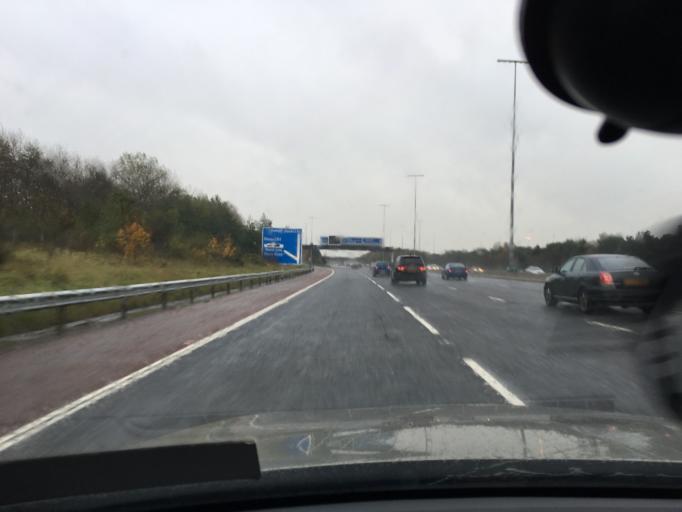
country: GB
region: Northern Ireland
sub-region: Newtownabbey District
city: Newtownabbey
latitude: 54.6353
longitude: -5.9191
